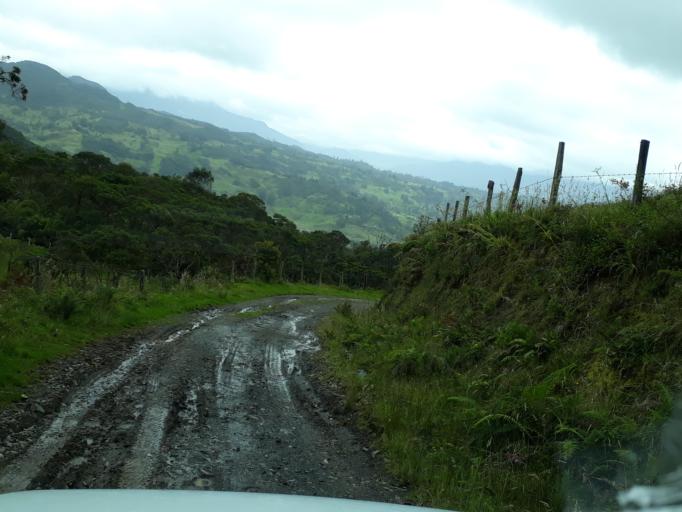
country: CO
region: Cundinamarca
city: Junin
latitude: 4.7345
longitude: -73.6254
